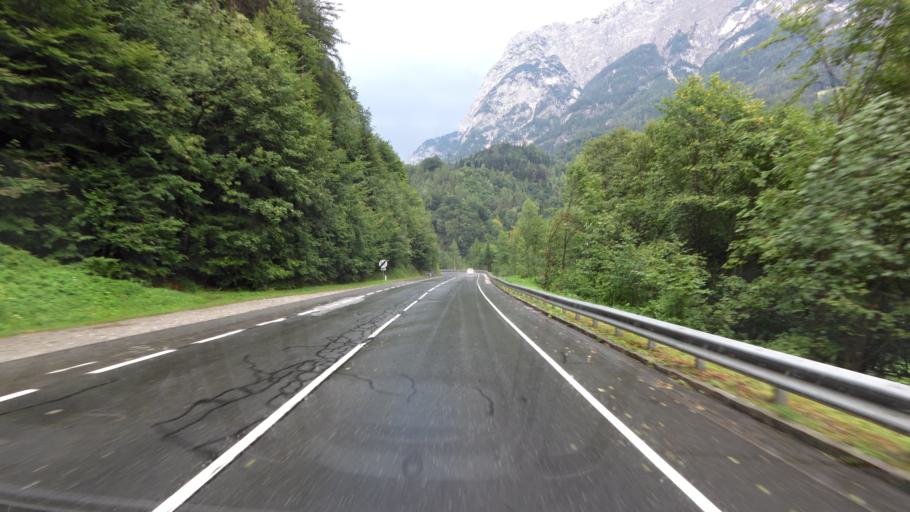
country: AT
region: Salzburg
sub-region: Politischer Bezirk Sankt Johann im Pongau
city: Werfen
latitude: 47.4844
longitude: 13.1855
